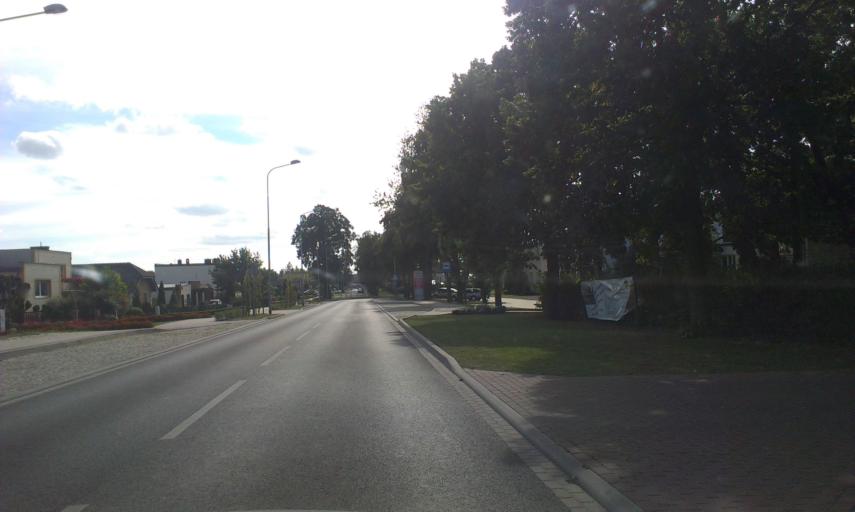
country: PL
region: Greater Poland Voivodeship
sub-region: Powiat zlotowski
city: Zlotow
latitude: 53.3747
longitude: 17.0208
